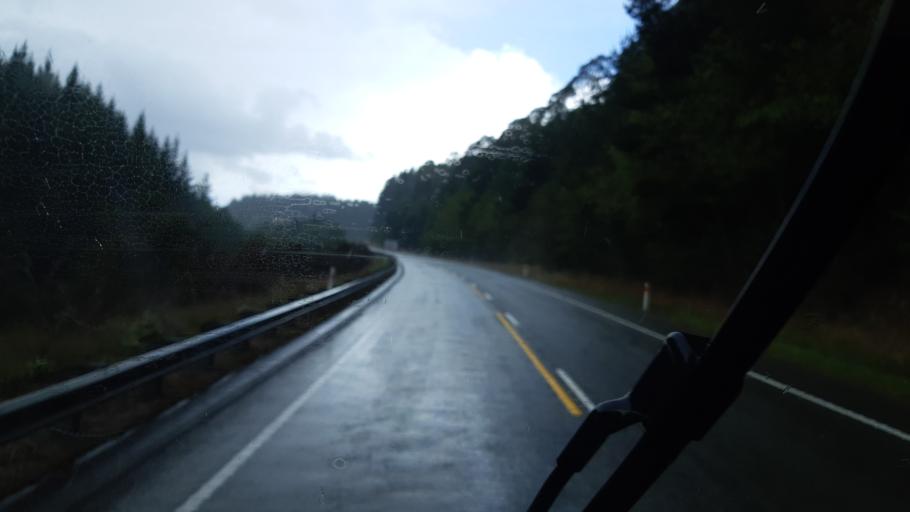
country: NZ
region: Tasman
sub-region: Tasman District
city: Wakefield
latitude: -41.4879
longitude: 172.8976
